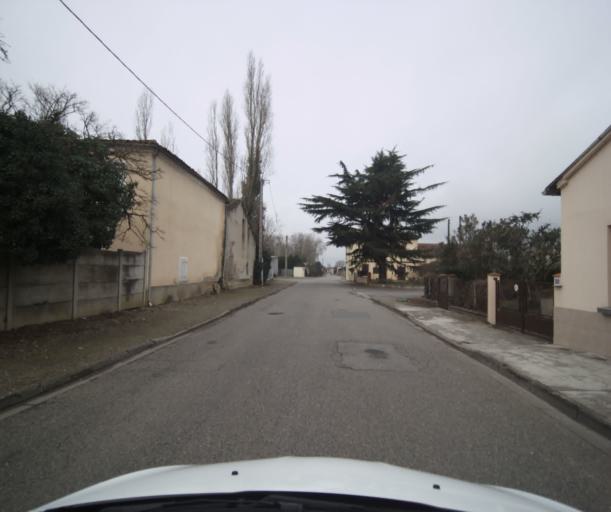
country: FR
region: Midi-Pyrenees
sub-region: Departement du Tarn-et-Garonne
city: Castelsarrasin
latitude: 44.0468
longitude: 1.1133
